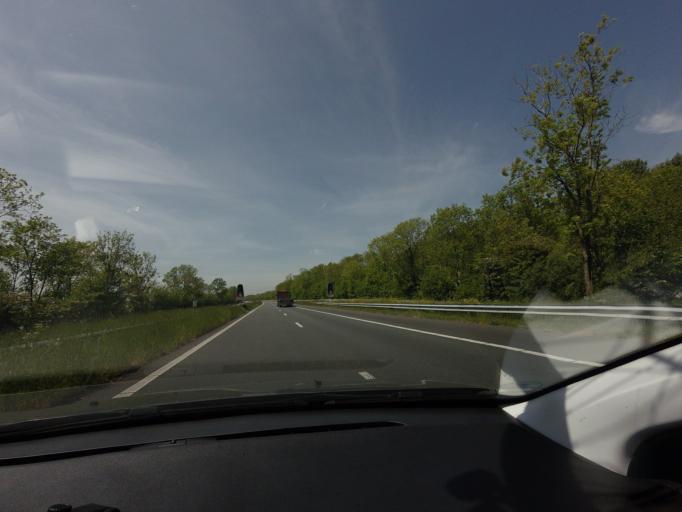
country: NL
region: Friesland
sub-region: Sudwest Fryslan
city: Bolsward
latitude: 53.0563
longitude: 5.5335
